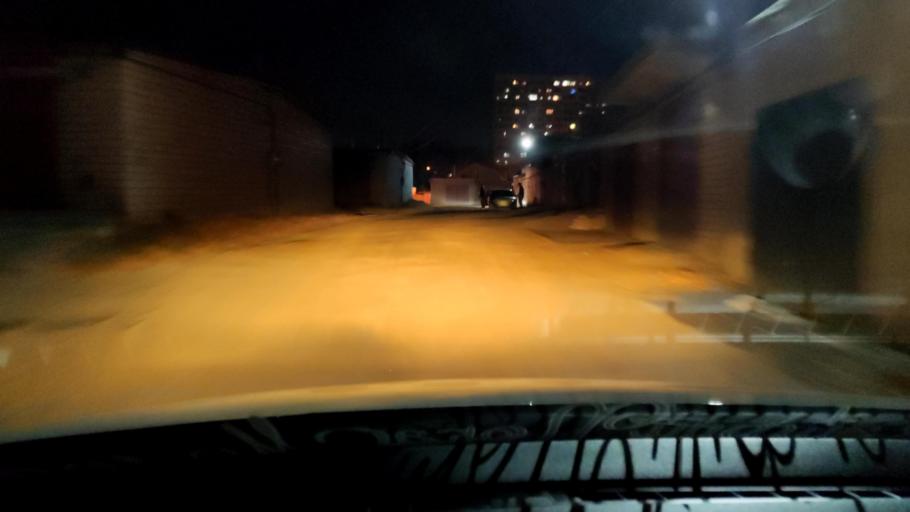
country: RU
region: Voronezj
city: Pridonskoy
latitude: 51.6889
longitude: 39.0770
